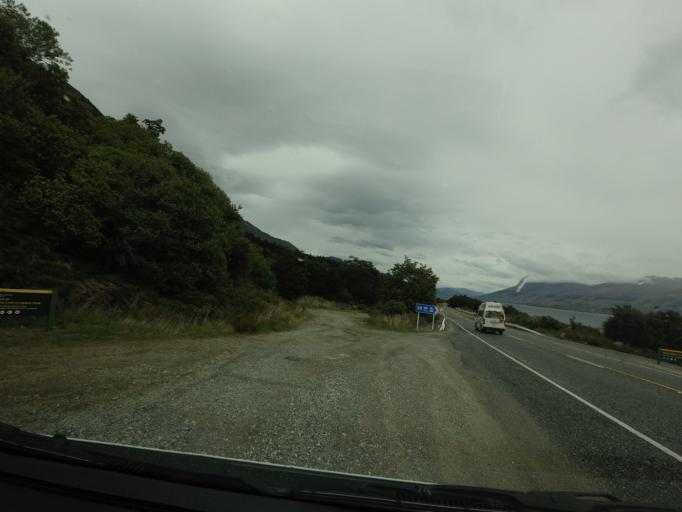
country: NZ
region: Otago
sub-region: Queenstown-Lakes District
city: Wanaka
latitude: -44.3518
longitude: 169.1702
